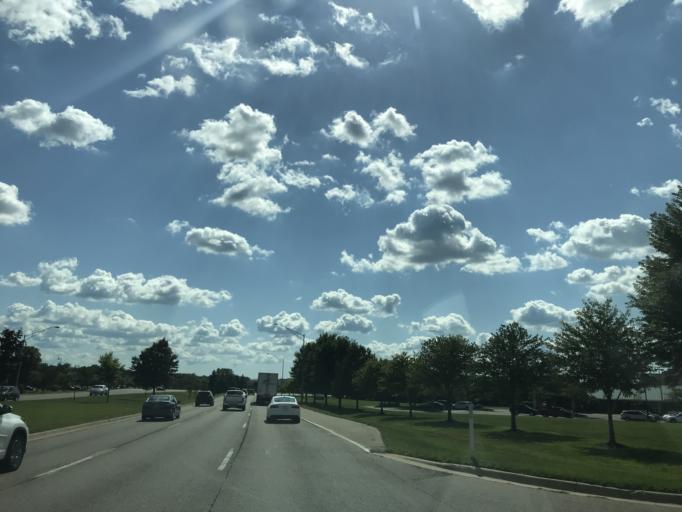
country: US
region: Michigan
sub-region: Kent County
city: Grandville
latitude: 42.8843
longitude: -85.7458
